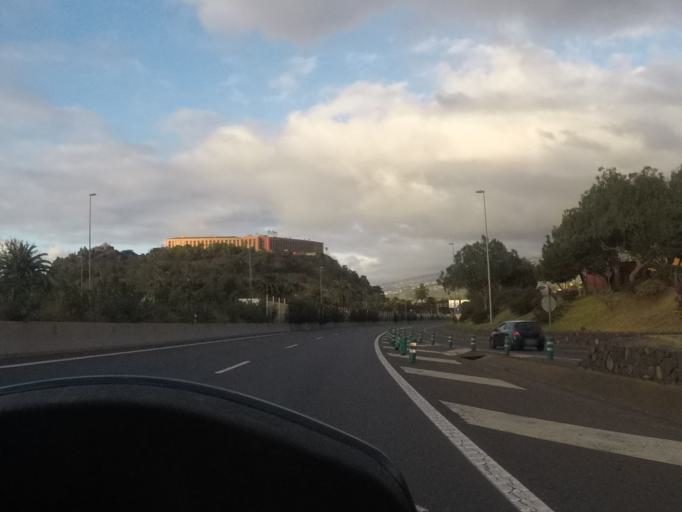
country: ES
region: Canary Islands
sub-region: Provincia de Santa Cruz de Tenerife
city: Puerto de la Cruz
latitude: 28.3964
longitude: -16.5498
